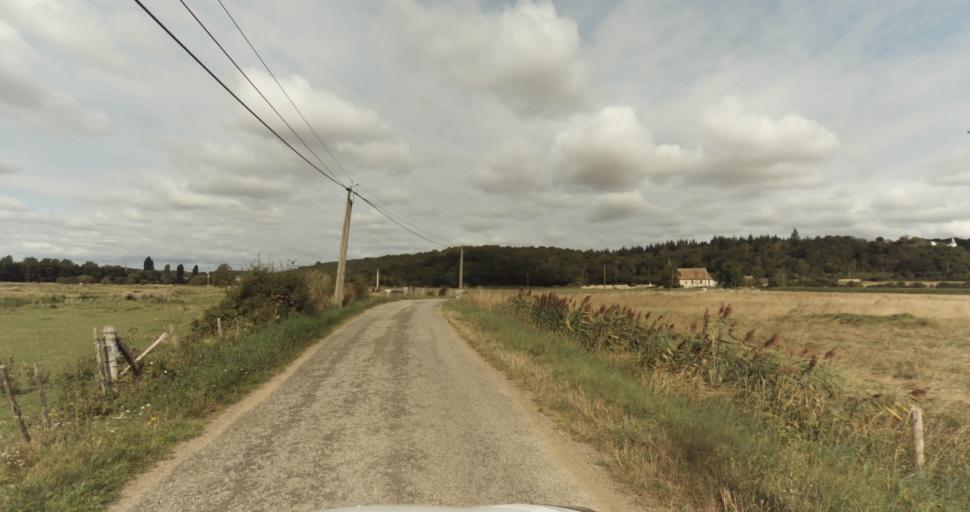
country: FR
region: Haute-Normandie
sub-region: Departement de l'Eure
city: Tillieres-sur-Avre
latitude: 48.7624
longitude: 1.1042
